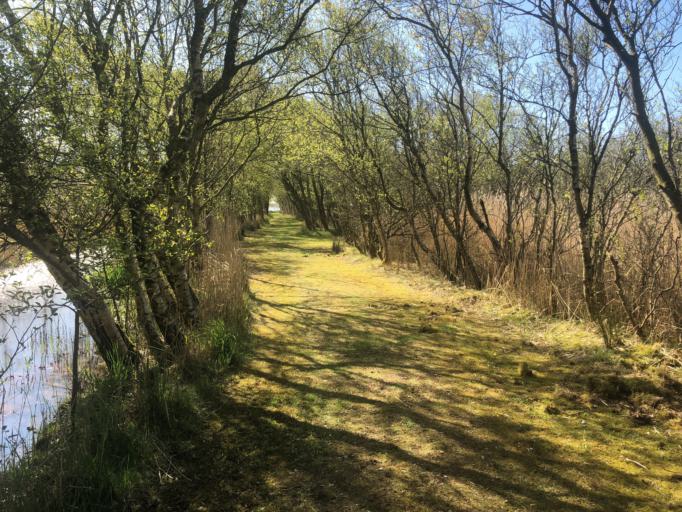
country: DK
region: Central Jutland
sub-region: Holstebro Kommune
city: Vinderup
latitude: 56.5704
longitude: 8.7909
